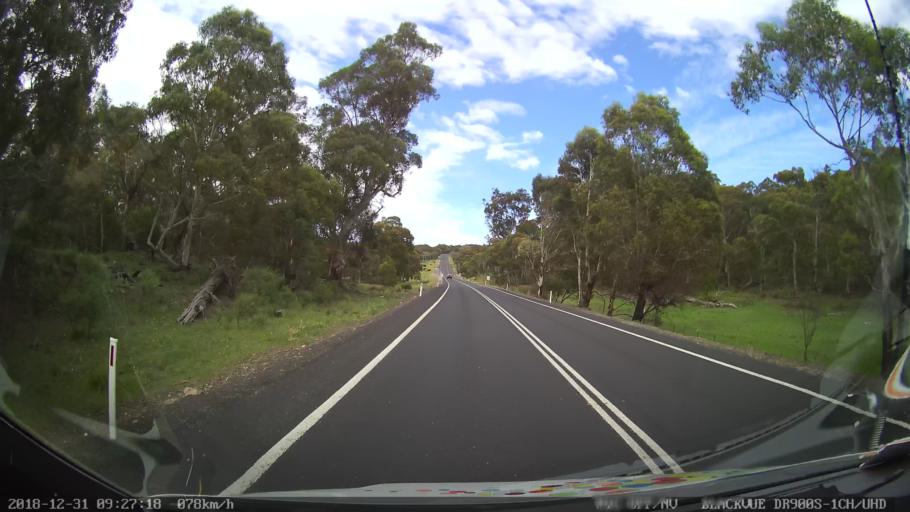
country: AU
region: New South Wales
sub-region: Snowy River
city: Jindabyne
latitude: -36.4553
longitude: 148.4863
